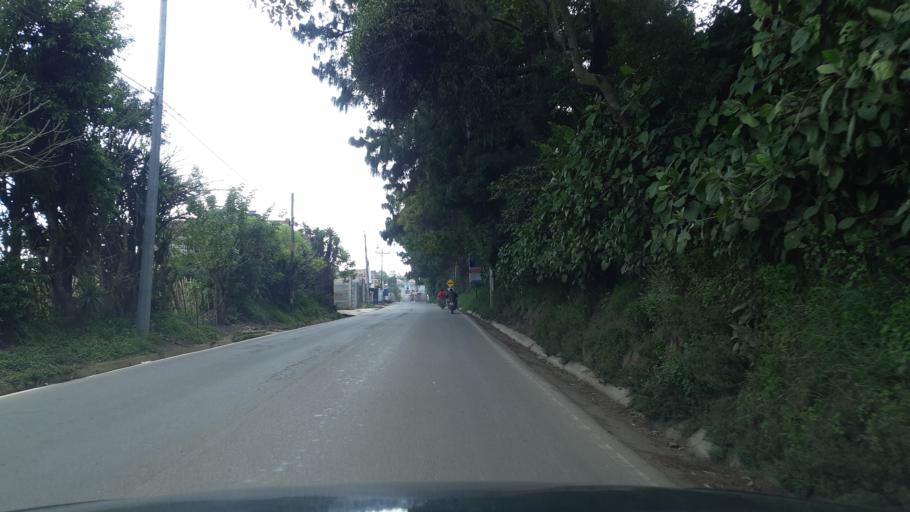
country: GT
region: Chimaltenango
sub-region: Municipio de Chimaltenango
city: Chimaltenango
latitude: 14.6680
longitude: -90.8078
